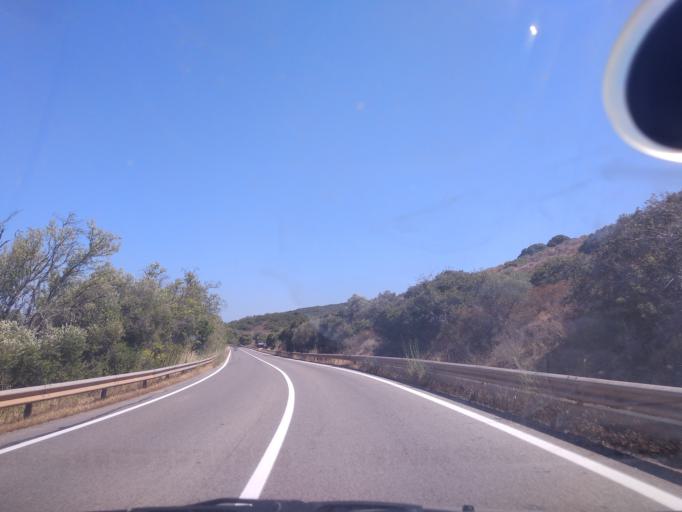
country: PT
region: Faro
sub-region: Lagos
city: Lagos
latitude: 37.1518
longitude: -8.7202
